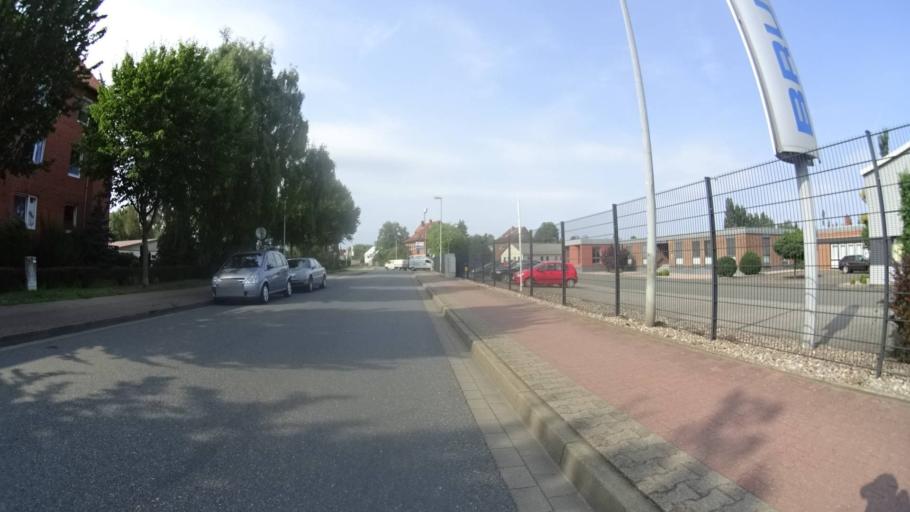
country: DE
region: Lower Saxony
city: Lueneburg
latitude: 53.2682
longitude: 10.4177
